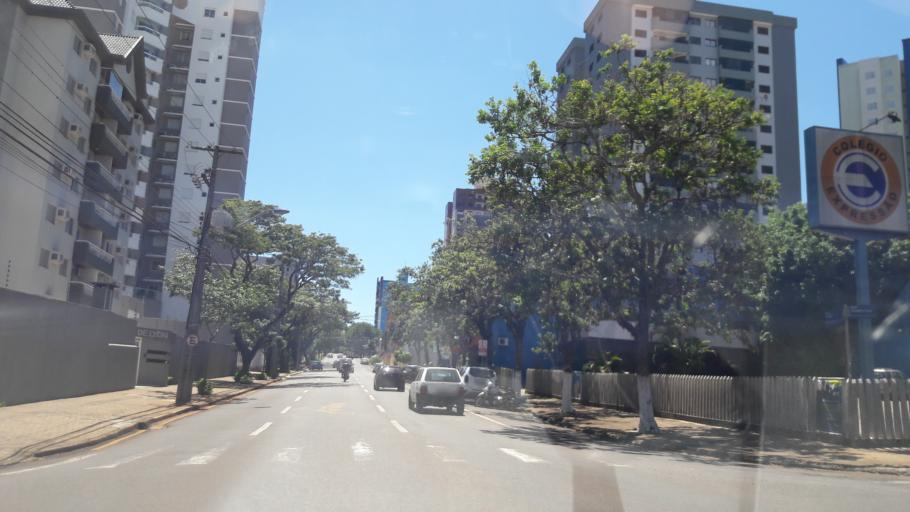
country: BR
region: Parana
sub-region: Cascavel
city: Cascavel
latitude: -24.9517
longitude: -53.4678
